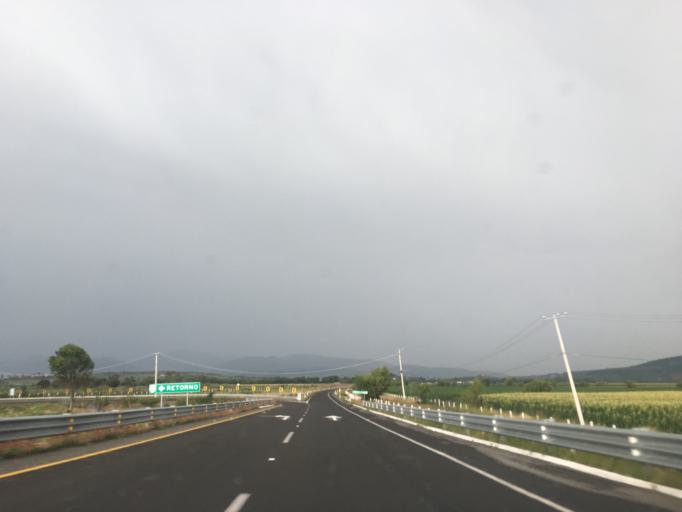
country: MX
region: Michoacan
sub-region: Alvaro Obregon
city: Lazaro Cardenas (La Purisima)
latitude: 19.8460
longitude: -101.0107
